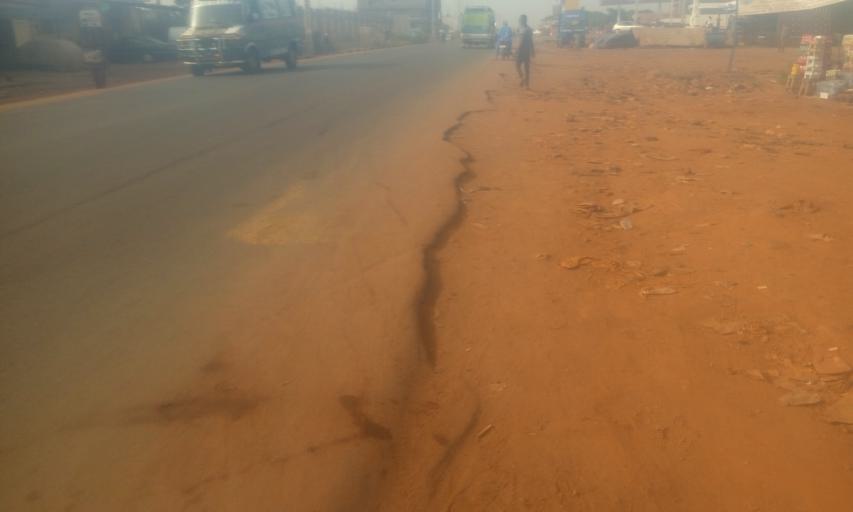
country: ML
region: Bamako
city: Bamako
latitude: 12.5795
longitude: -8.0738
